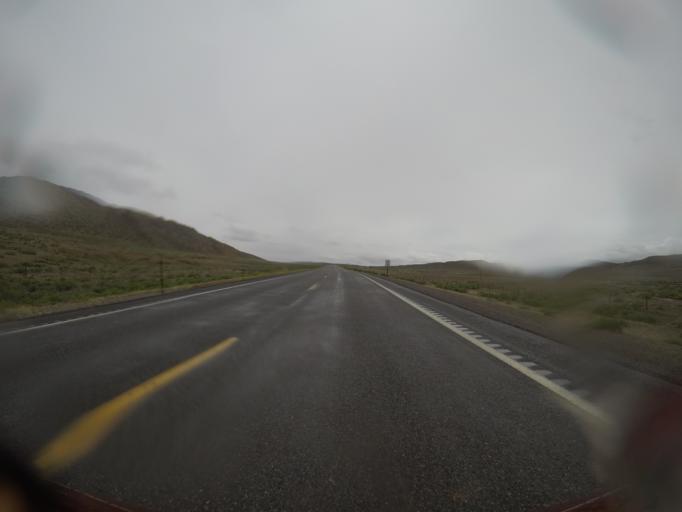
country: US
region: Wyoming
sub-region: Big Horn County
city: Lovell
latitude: 44.9474
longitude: -108.2971
